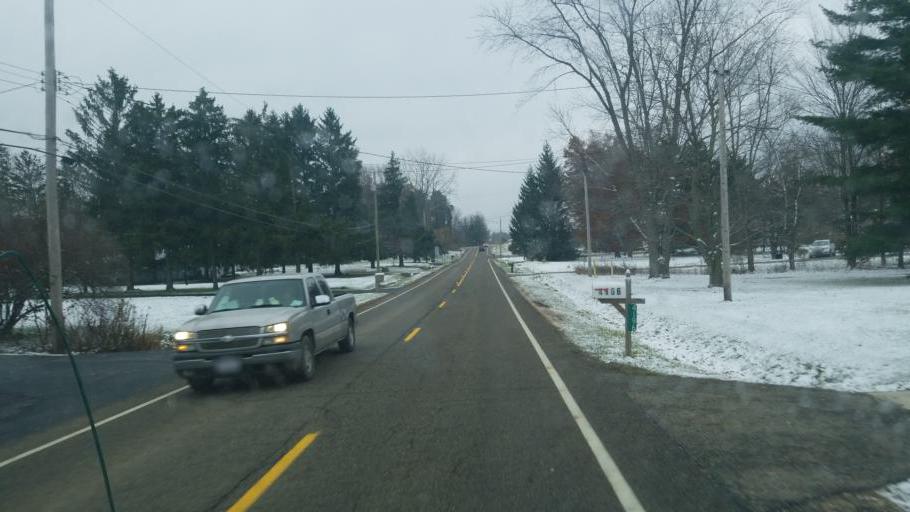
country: US
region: Ohio
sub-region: Cuyahoga County
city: Broadview Heights
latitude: 41.2773
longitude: -81.6654
